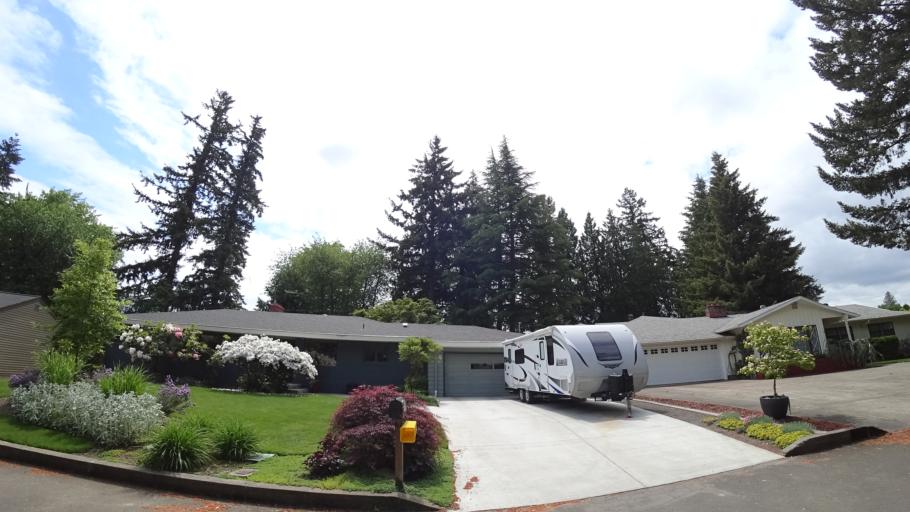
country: US
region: Oregon
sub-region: Washington County
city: Garden Home-Whitford
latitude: 45.4626
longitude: -122.7758
